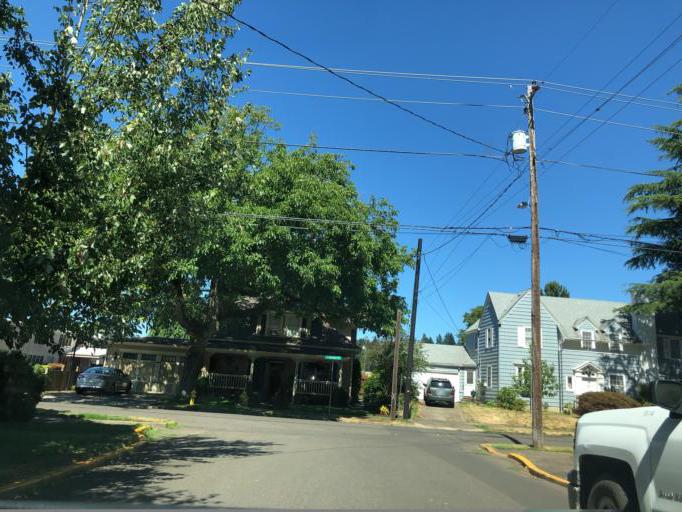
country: US
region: Oregon
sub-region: Marion County
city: Silverton
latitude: 45.0034
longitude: -122.7846
